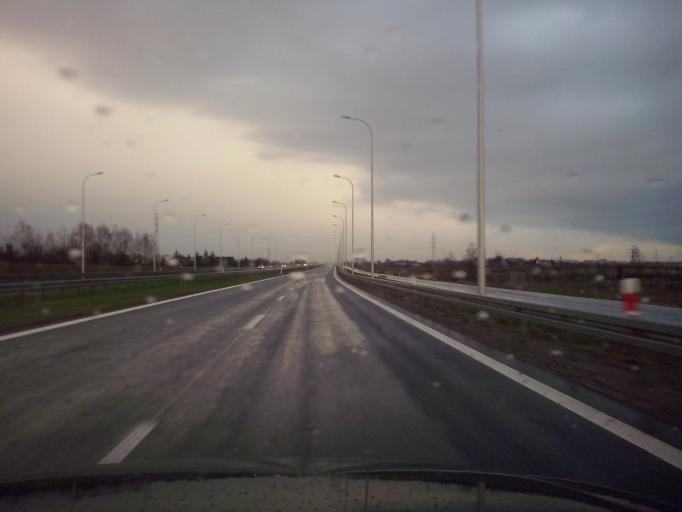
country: PL
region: Lublin Voivodeship
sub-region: Powiat lubelski
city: Jastkow
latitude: 51.2754
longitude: 22.4748
